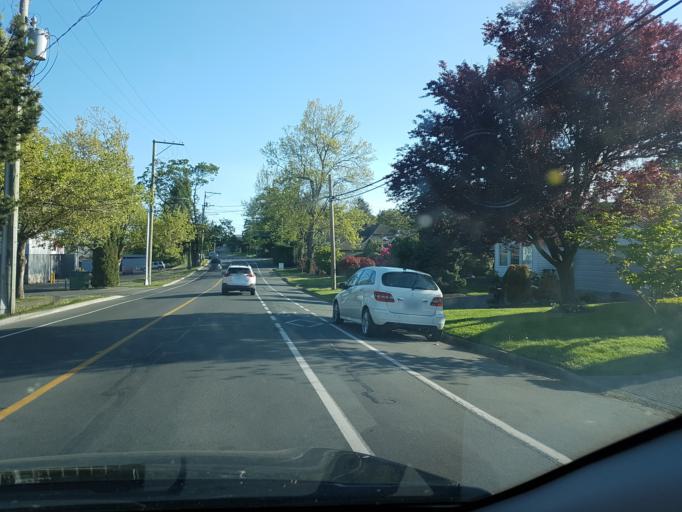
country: CA
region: British Columbia
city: Oak Bay
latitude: 48.4729
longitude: -123.3345
